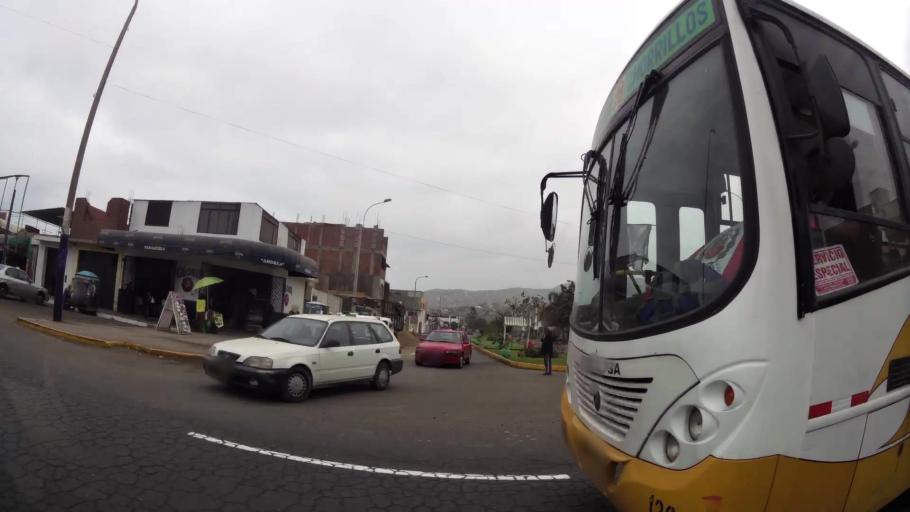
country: PE
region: Lima
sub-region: Lima
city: Surco
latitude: -12.2027
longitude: -77.0153
